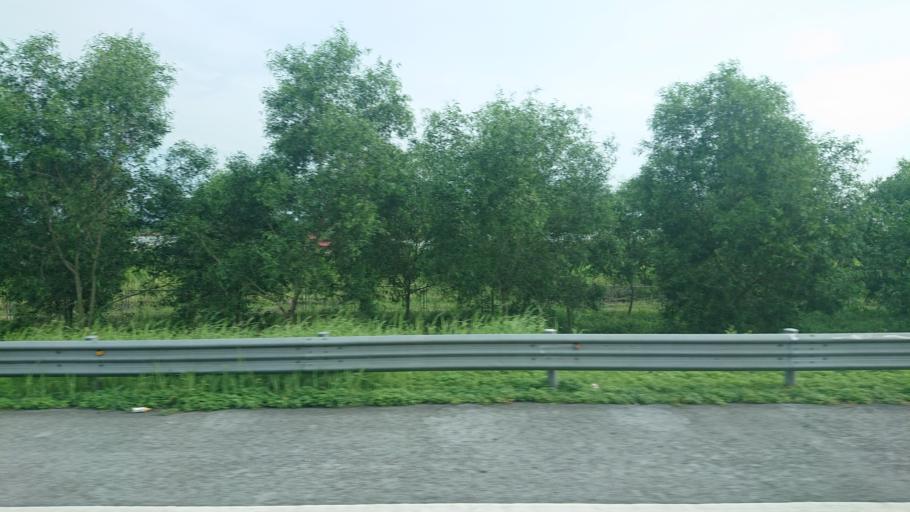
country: VN
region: Hai Phong
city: An Lao
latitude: 20.8001
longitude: 106.5339
